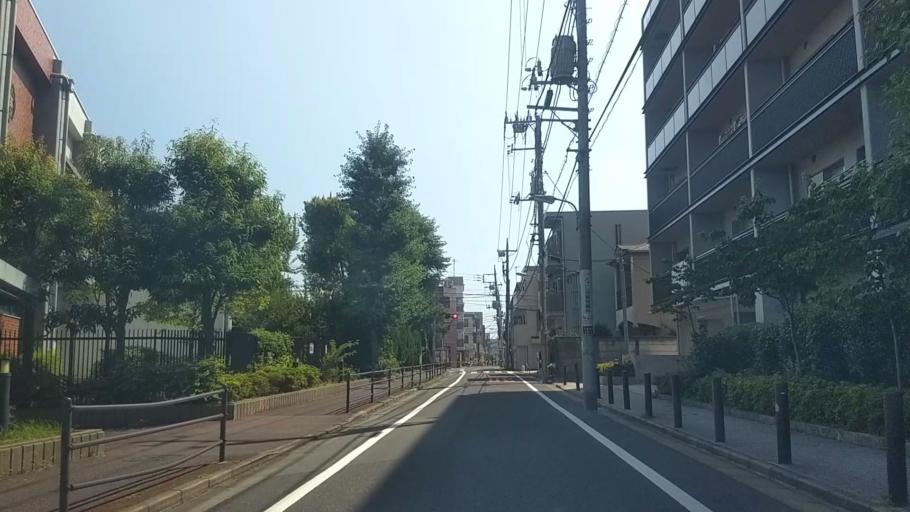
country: JP
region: Tokyo
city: Tokyo
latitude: 35.6097
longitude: 139.7202
